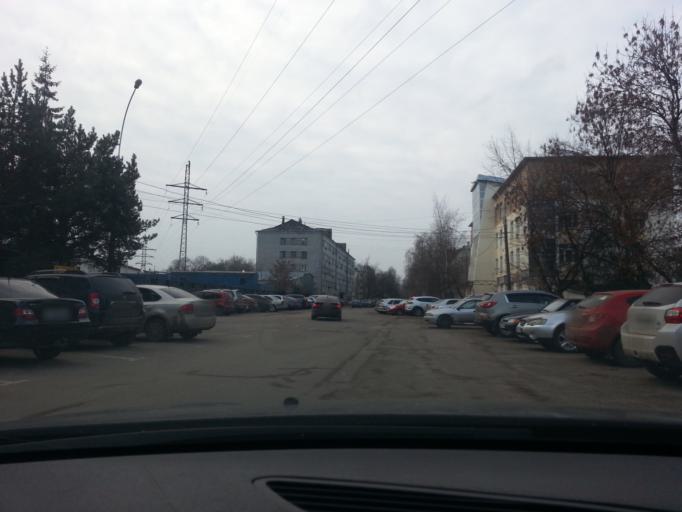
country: RU
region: Vologda
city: Vologda
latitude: 59.2262
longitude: 39.9132
